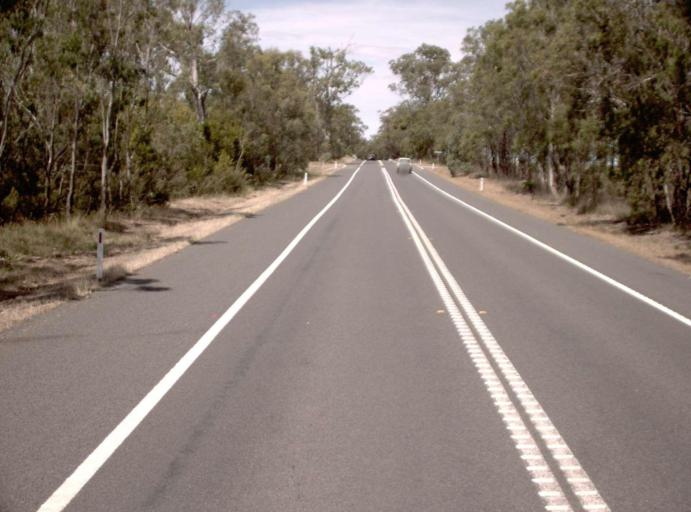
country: AU
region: Victoria
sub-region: Wellington
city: Sale
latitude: -37.9426
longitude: 147.1379
